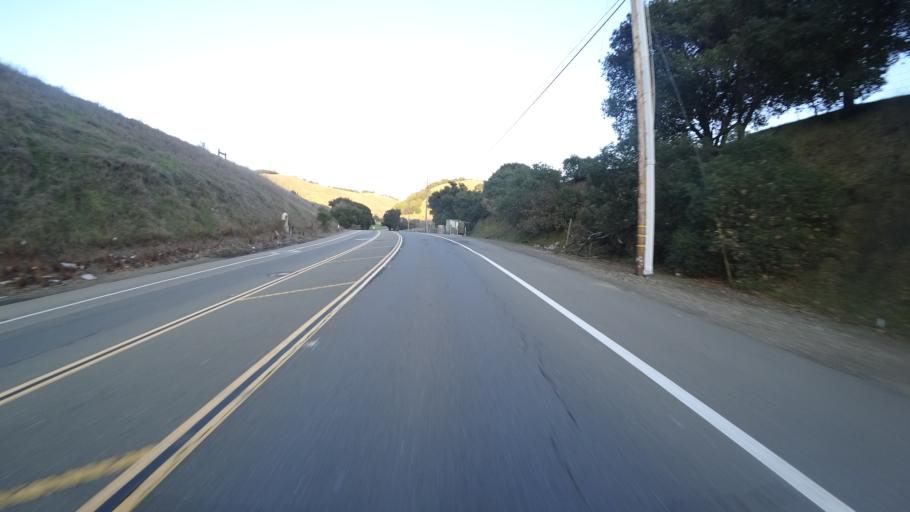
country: US
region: California
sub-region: Alameda County
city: Fairview
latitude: 37.6981
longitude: -122.0246
